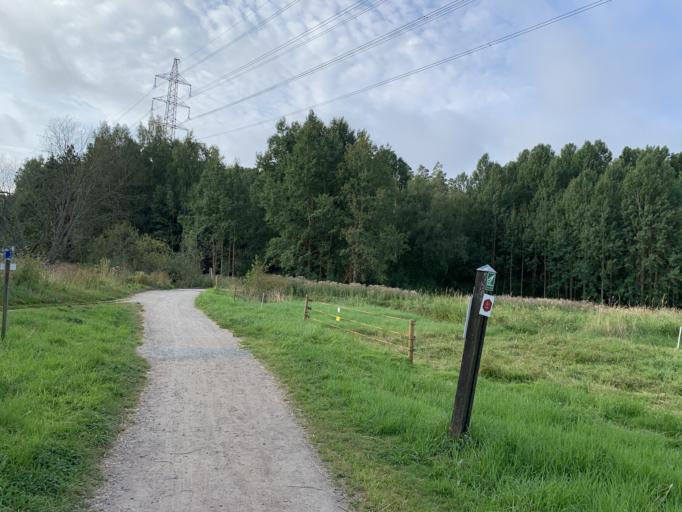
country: SE
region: Stockholm
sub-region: Solna Kommun
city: Rasunda
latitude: 59.3918
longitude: 17.9866
